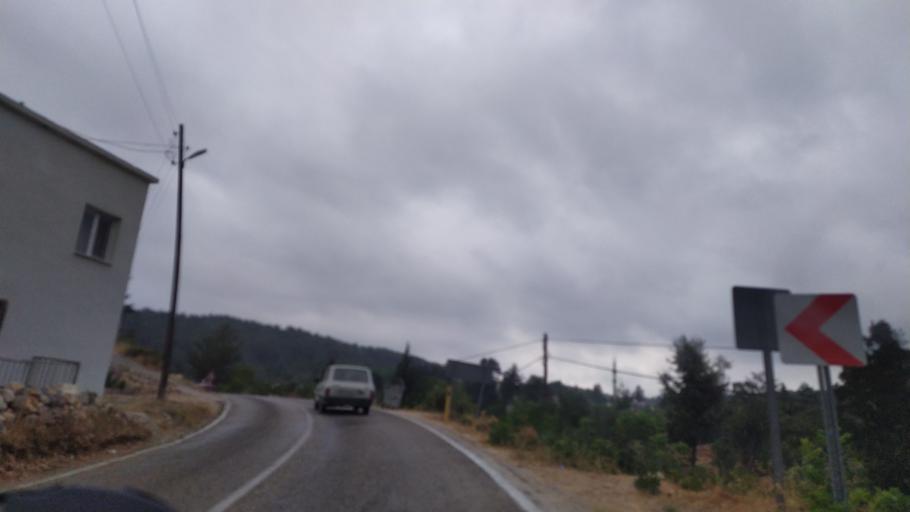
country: TR
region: Mersin
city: Silifke
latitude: 36.5357
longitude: 33.9422
